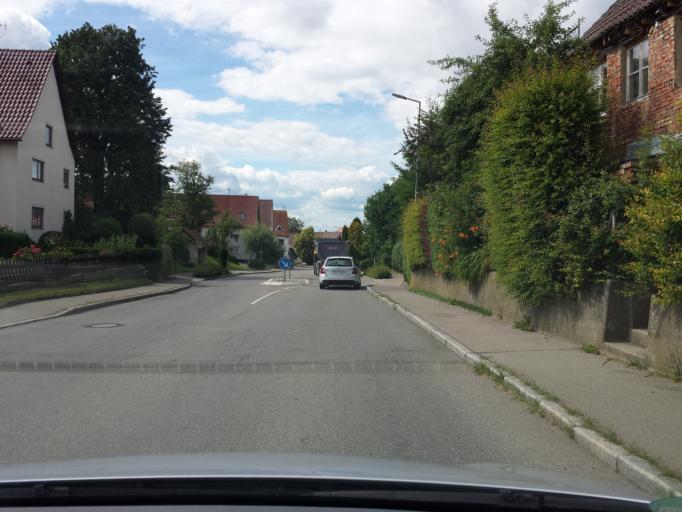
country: DE
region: Baden-Wuerttemberg
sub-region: Tuebingen Region
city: Burgrieden
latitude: 48.2239
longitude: 9.9536
